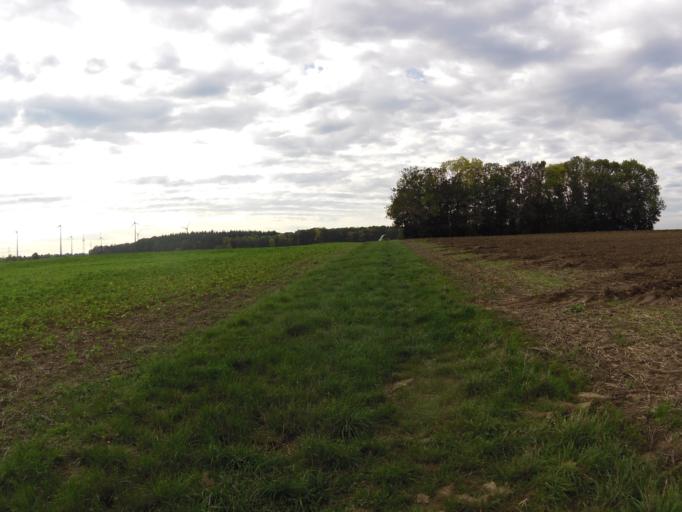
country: DE
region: Bavaria
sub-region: Regierungsbezirk Unterfranken
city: Biebelried
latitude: 49.7304
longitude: 10.0769
